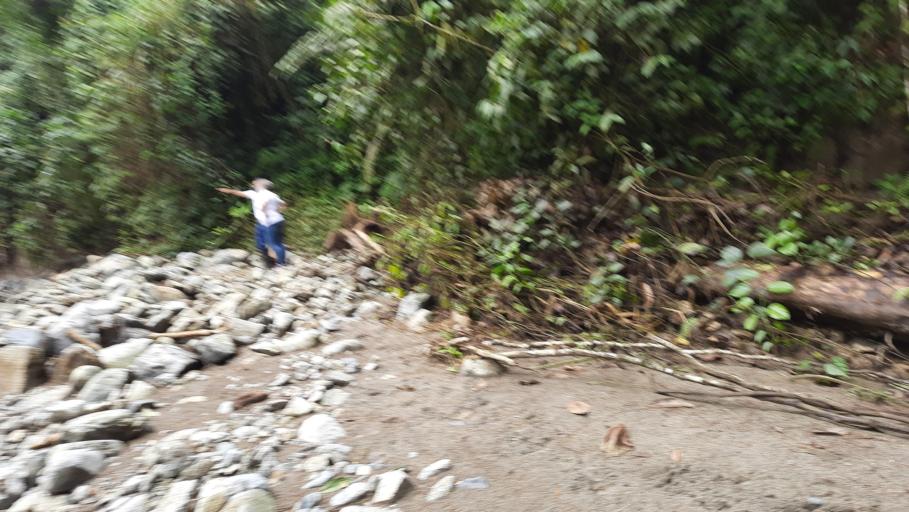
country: CO
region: Valle del Cauca
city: Buga
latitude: 3.8532
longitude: -76.1849
